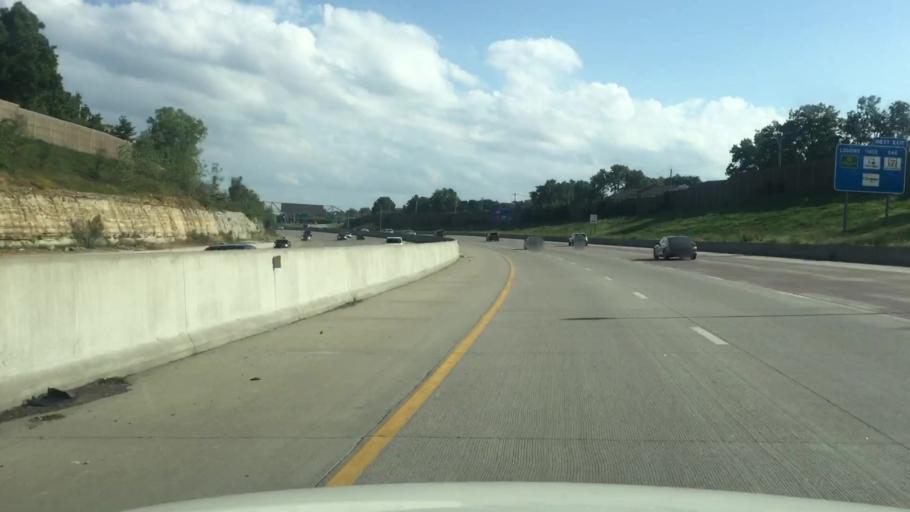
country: US
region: Kansas
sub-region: Johnson County
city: Lenexa
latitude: 38.9629
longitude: -94.7136
